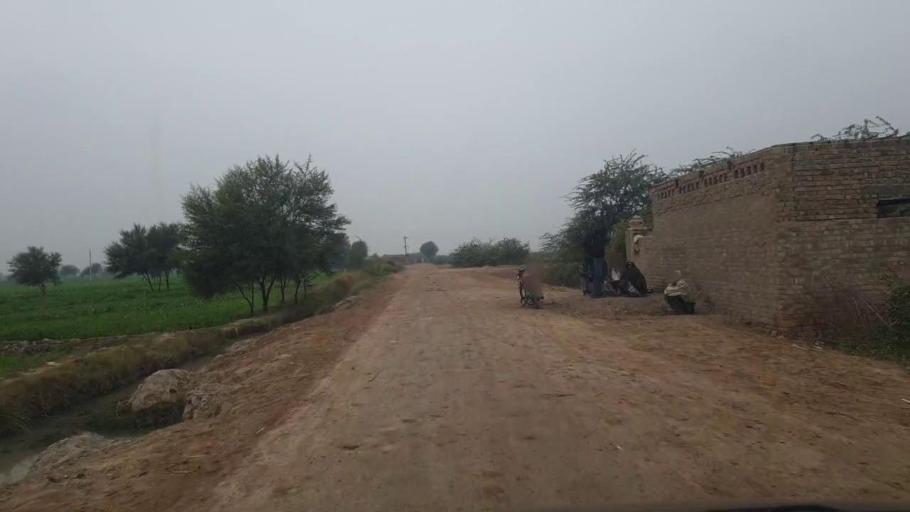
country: PK
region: Sindh
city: Tando Adam
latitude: 25.8290
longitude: 68.6774
